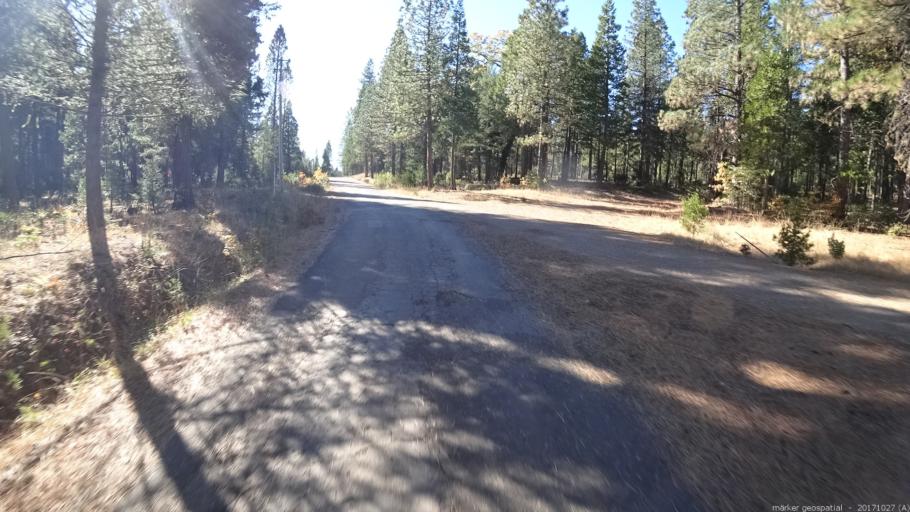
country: US
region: California
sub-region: Shasta County
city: Shingletown
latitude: 40.6146
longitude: -121.8184
